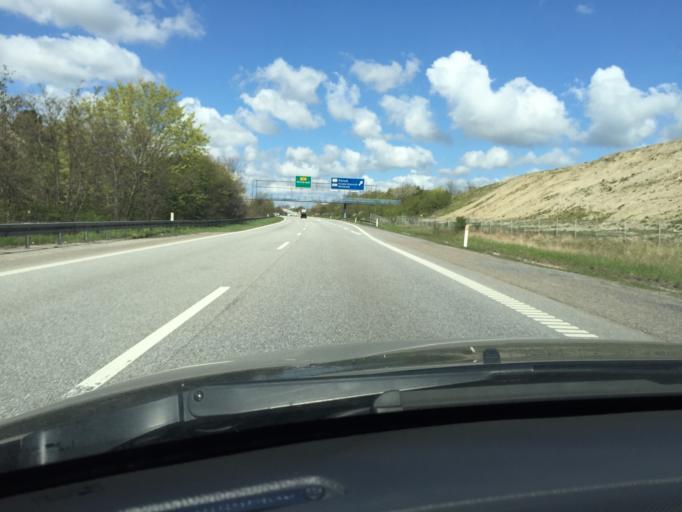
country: DK
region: Capital Region
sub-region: Fureso Kommune
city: Stavnsholt
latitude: 55.8194
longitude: 12.3832
